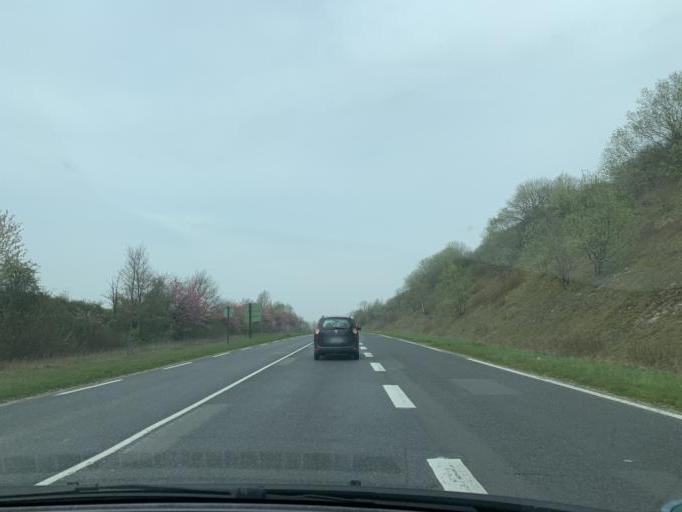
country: FR
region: Nord-Pas-de-Calais
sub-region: Departement du Pas-de-Calais
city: Montreuil
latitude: 50.4578
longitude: 1.7691
